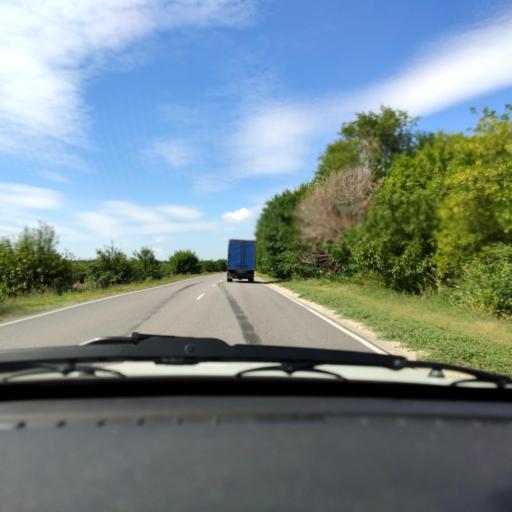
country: RU
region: Voronezj
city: Volya
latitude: 51.7011
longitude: 39.5152
